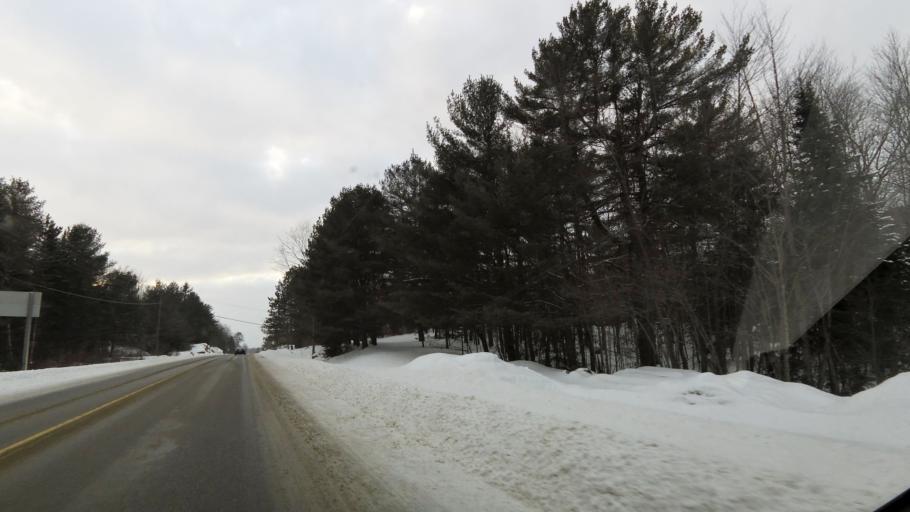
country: CA
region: Ontario
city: Omemee
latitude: 44.7256
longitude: -78.8160
